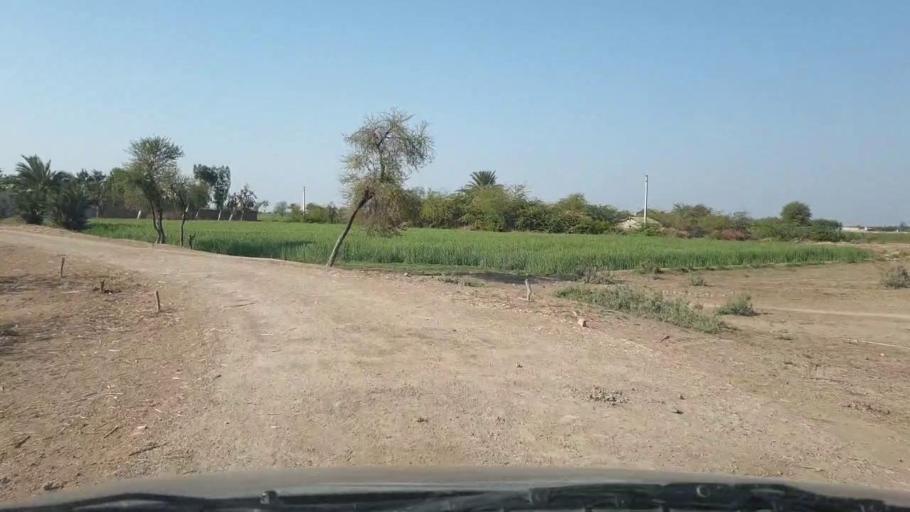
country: PK
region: Sindh
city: Samaro
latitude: 25.1768
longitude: 69.2833
